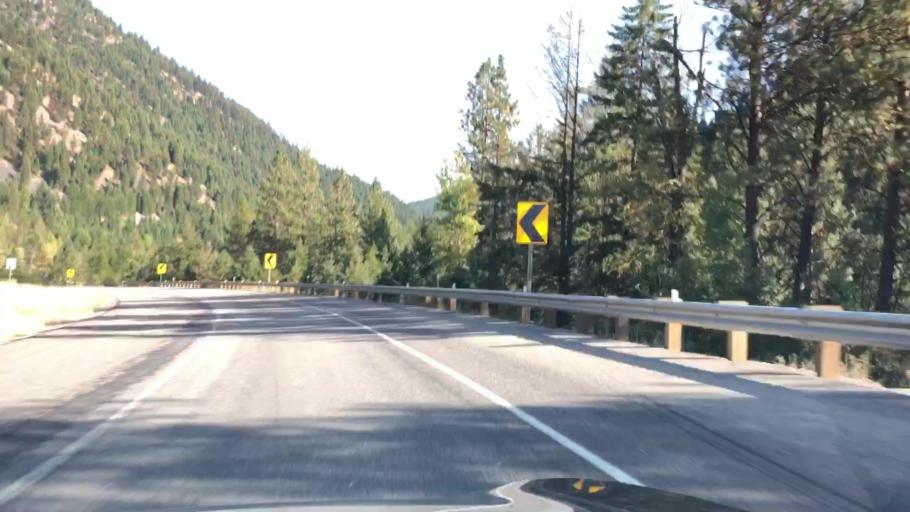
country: US
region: Montana
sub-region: Sanders County
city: Thompson Falls
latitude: 47.3277
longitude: -115.2564
